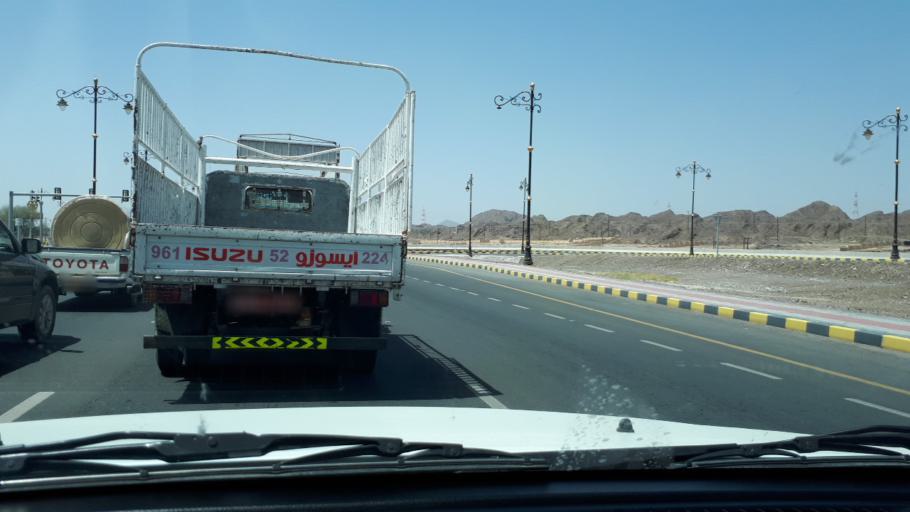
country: OM
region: Muhafazat ad Dakhiliyah
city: Nizwa
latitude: 22.8898
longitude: 57.5275
